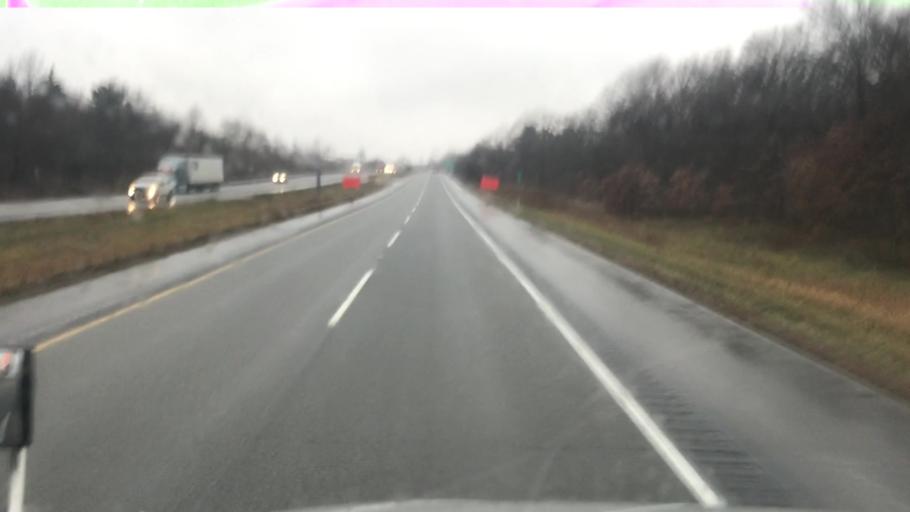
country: US
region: Indiana
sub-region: Saint Joseph County
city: Georgetown
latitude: 41.7166
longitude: -86.2295
